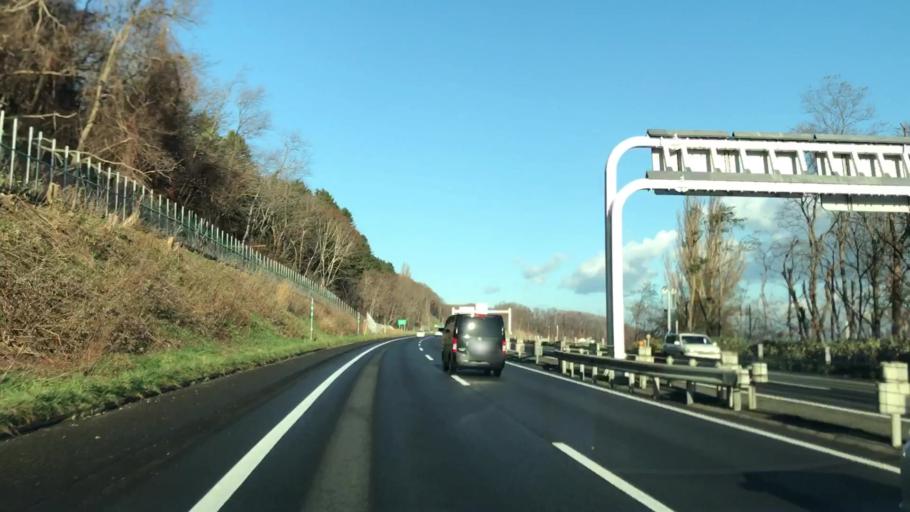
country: JP
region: Hokkaido
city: Sapporo
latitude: 43.0951
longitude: 141.2536
